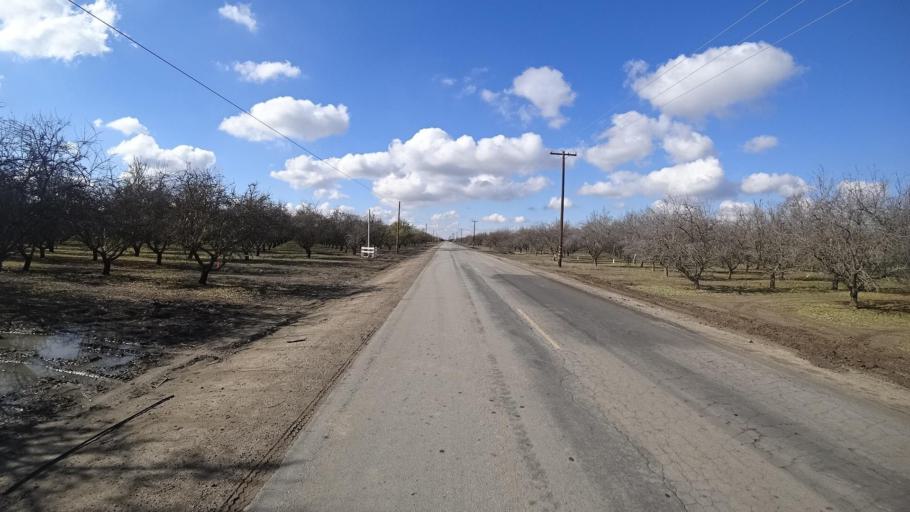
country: US
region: California
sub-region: Kern County
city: McFarland
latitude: 35.6887
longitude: -119.3161
